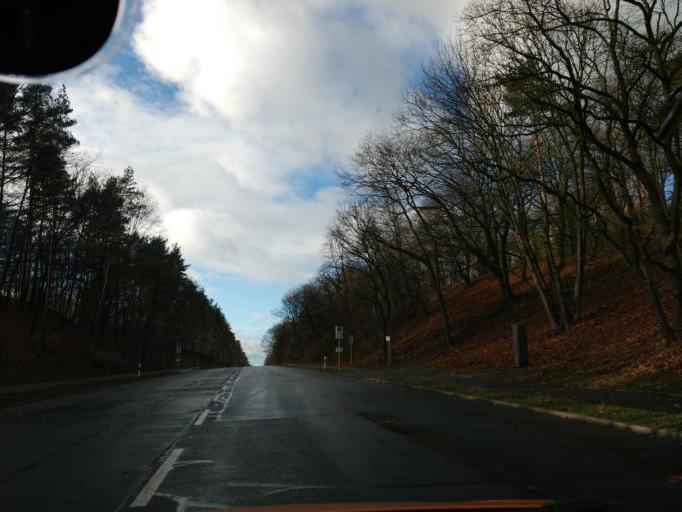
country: DE
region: Berlin
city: Wannsee
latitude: 52.4157
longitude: 13.1269
